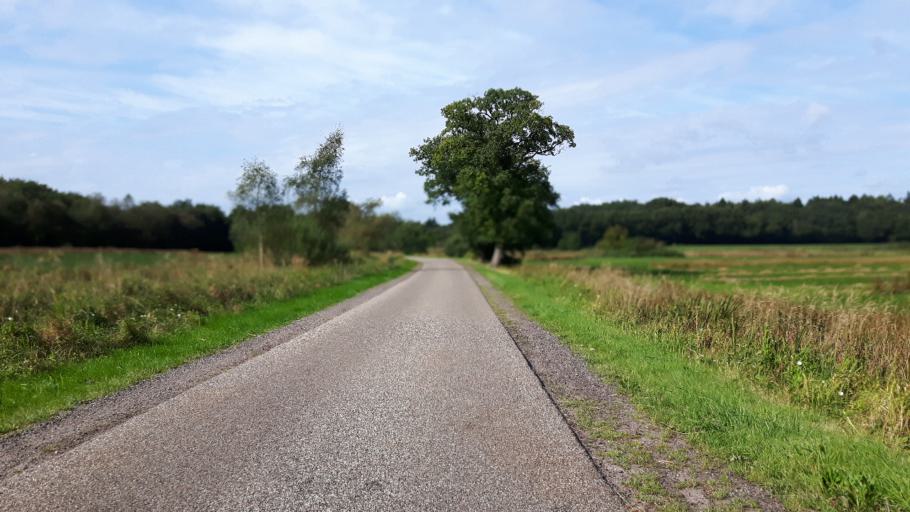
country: NL
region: Groningen
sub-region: Gemeente Leek
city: Leek
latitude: 53.1244
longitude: 6.4504
